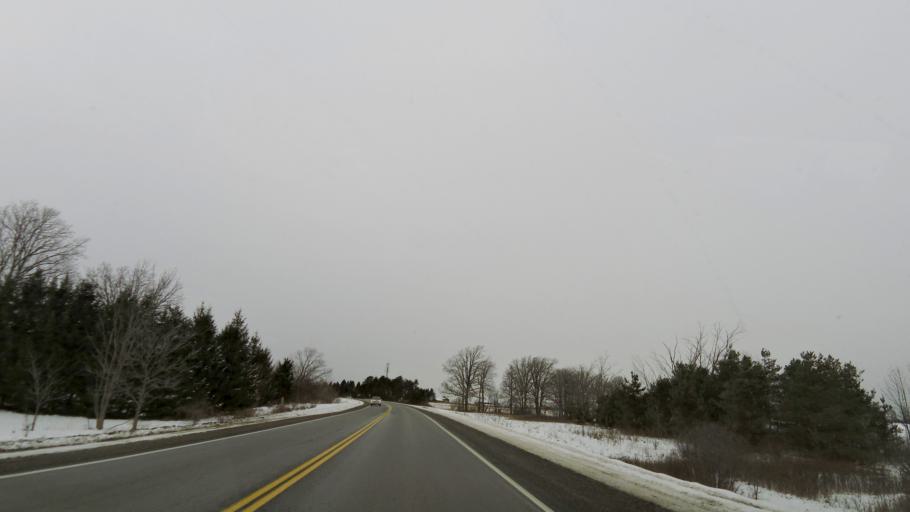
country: CA
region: Ontario
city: Cambridge
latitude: 43.3255
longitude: -80.2027
